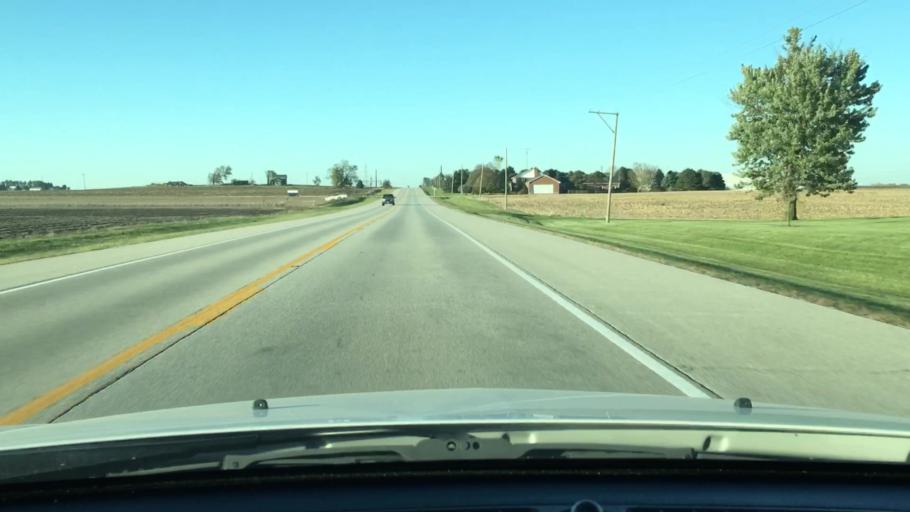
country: US
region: Illinois
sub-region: DeKalb County
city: Waterman
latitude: 41.8176
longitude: -88.7539
